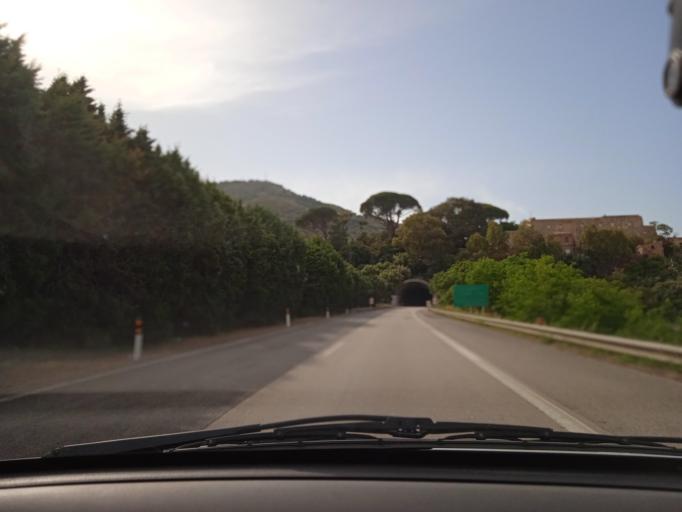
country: IT
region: Sicily
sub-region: Messina
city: Oliveri
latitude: 38.1202
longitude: 15.0577
